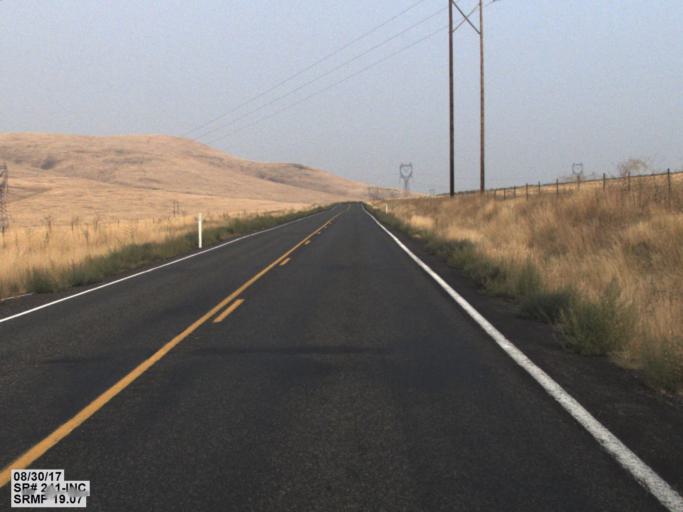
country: US
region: Washington
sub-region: Yakima County
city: Sunnyside
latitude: 46.4652
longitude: -119.9341
